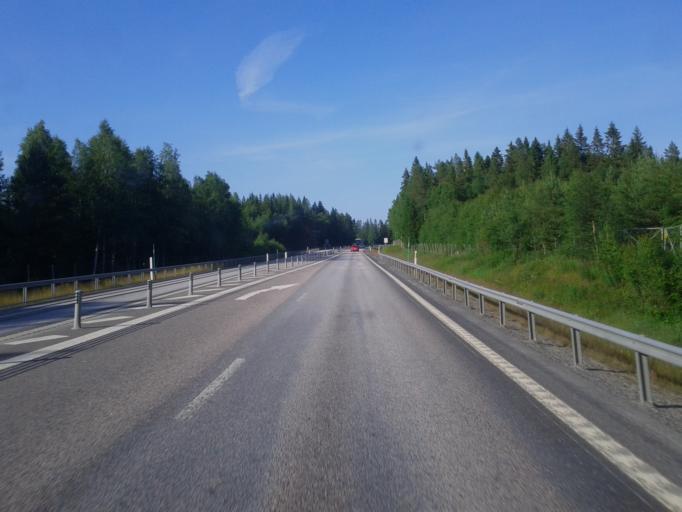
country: SE
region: Vaesterbotten
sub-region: Umea Kommun
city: Saevar
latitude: 63.9141
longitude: 20.5946
